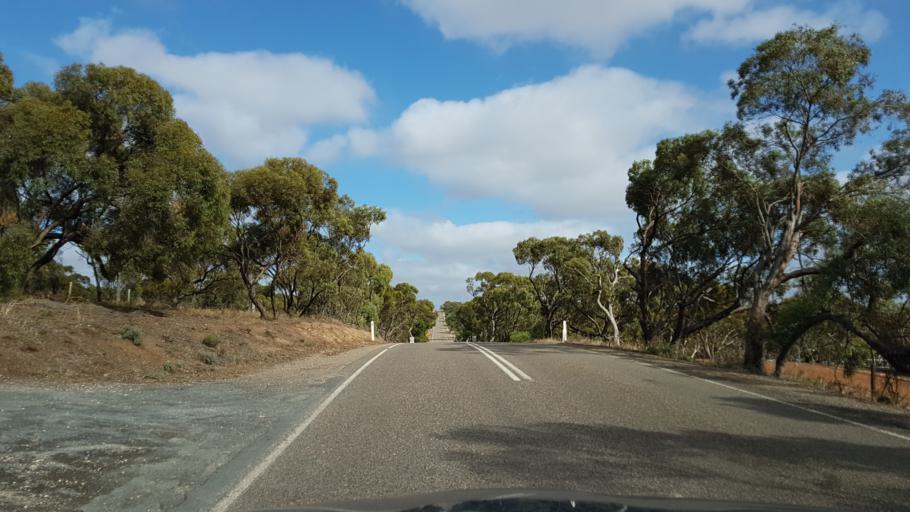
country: AU
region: South Australia
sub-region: Murray Bridge
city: Murray Bridge
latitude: -35.1163
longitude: 139.2329
